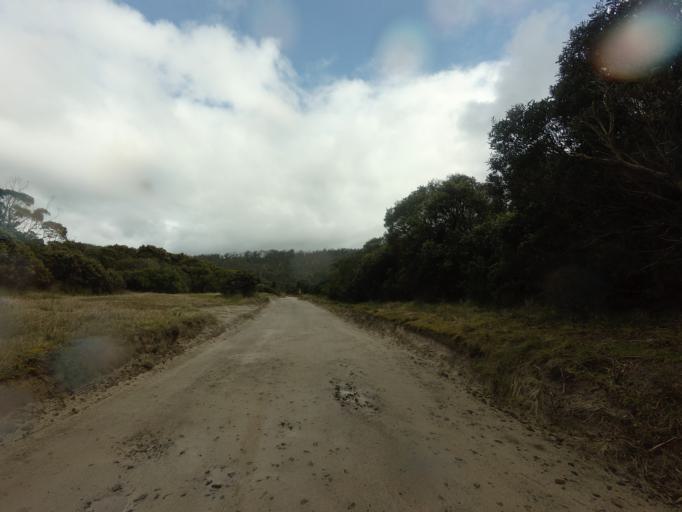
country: AU
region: Tasmania
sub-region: Huon Valley
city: Geeveston
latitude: -43.5816
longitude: 146.8901
